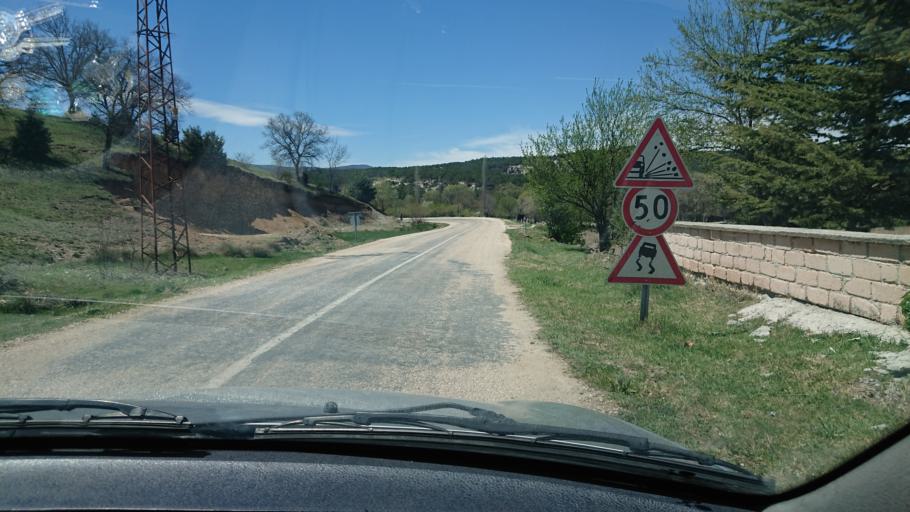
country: TR
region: Eskisehir
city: Eskisehir
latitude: 39.5391
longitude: 30.4464
